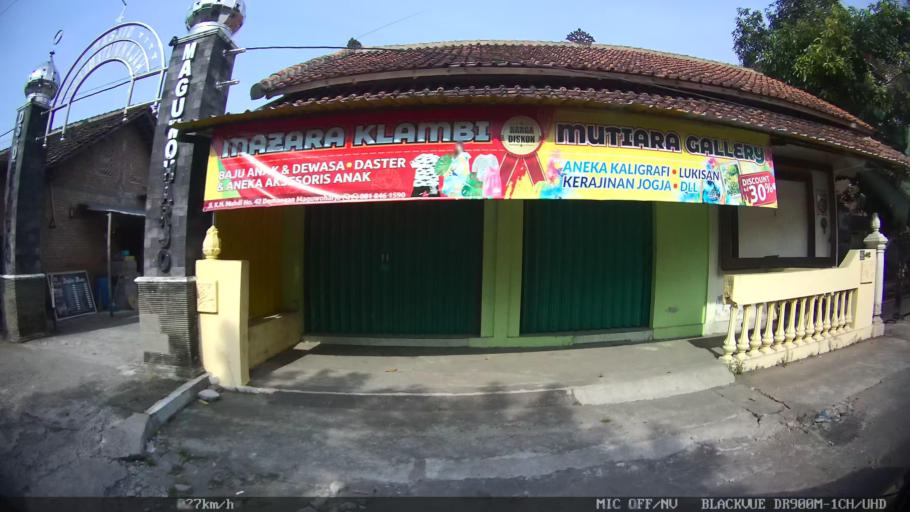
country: ID
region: Daerah Istimewa Yogyakarta
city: Depok
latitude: -7.7727
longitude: 110.4236
